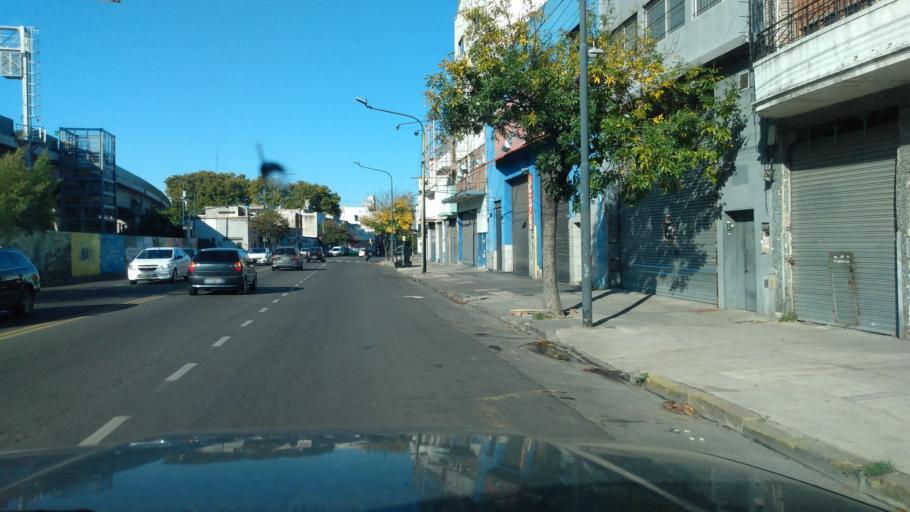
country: AR
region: Buenos Aires F.D.
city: Villa Santa Rita
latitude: -34.5966
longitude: -58.4602
